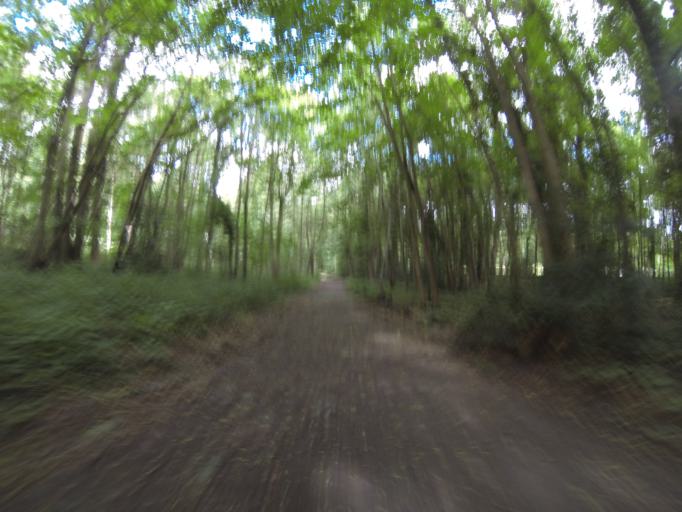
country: GB
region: England
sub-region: Greater London
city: Bexley
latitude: 51.4289
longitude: 0.1616
